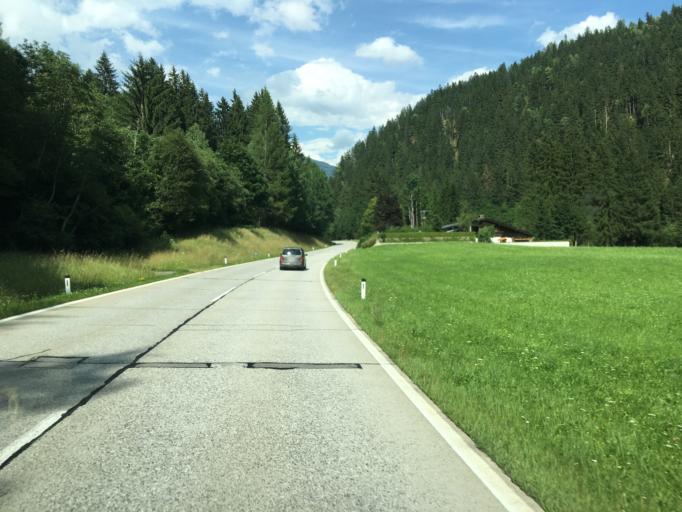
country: AT
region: Carinthia
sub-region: Politischer Bezirk Spittal an der Drau
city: Stall
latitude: 46.9246
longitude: 13.0768
